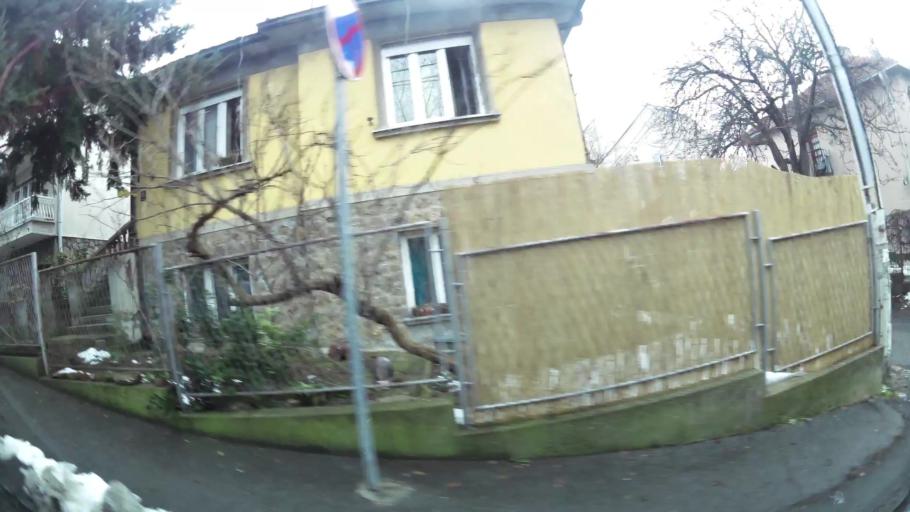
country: RS
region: Central Serbia
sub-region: Belgrade
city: Vozdovac
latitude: 44.7742
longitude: 20.4790
